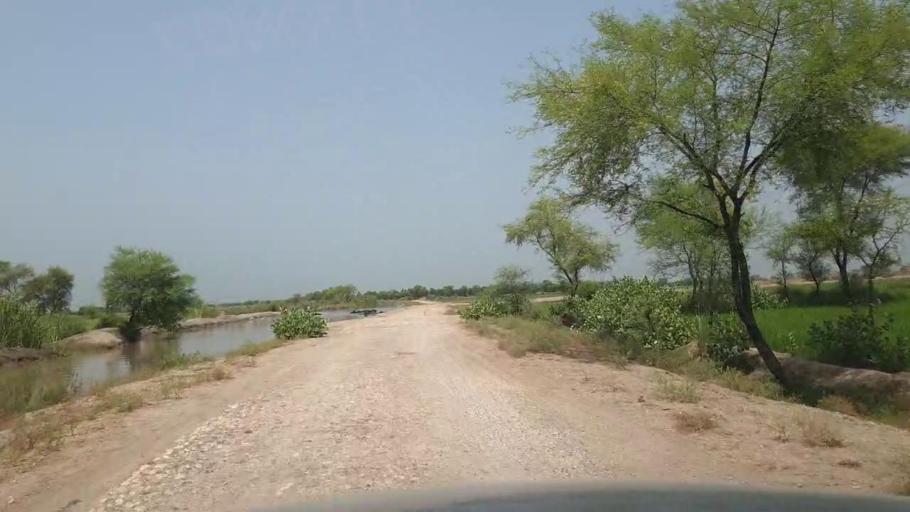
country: PK
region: Sindh
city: Garhi Yasin
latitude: 27.8371
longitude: 68.4919
